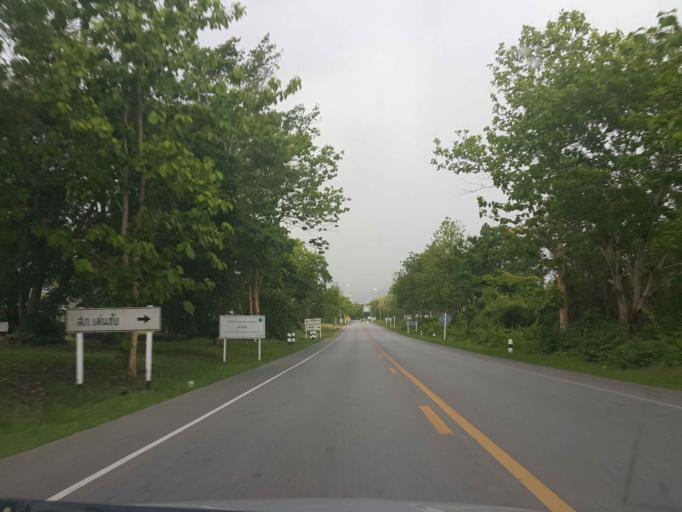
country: TH
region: Phrae
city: Den Chai
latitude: 17.9774
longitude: 100.0358
